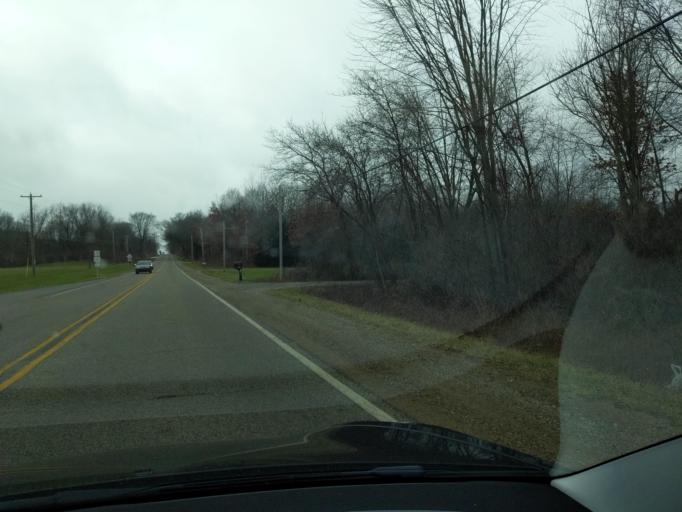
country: US
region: Michigan
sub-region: Jackson County
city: Spring Arbor
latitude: 42.2525
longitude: -84.5393
